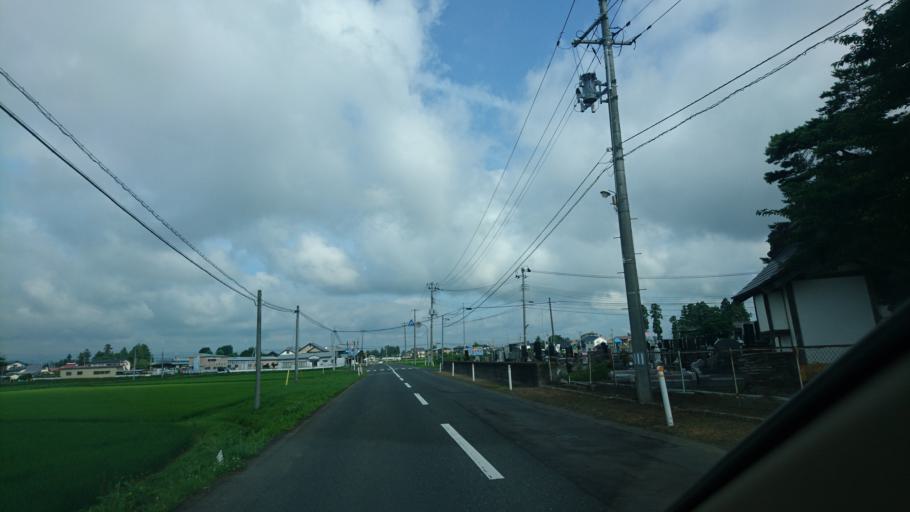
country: JP
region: Iwate
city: Mizusawa
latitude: 39.1701
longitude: 141.1734
